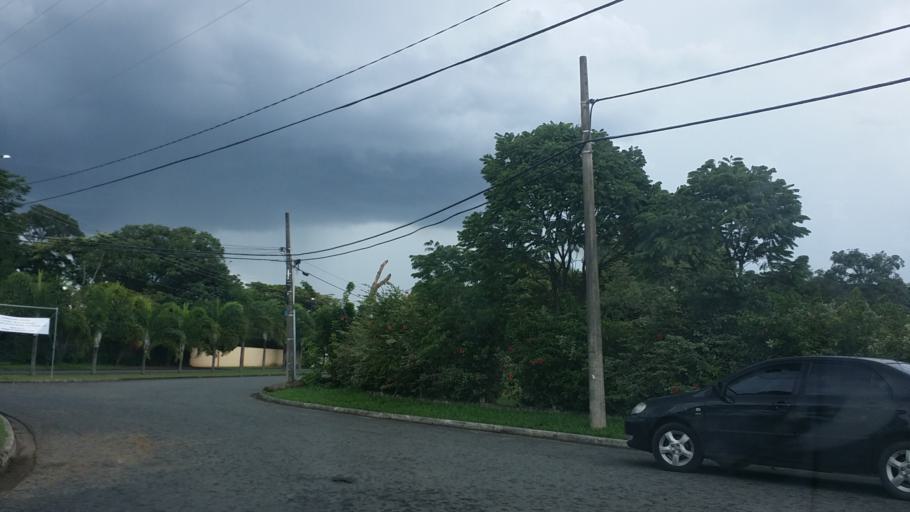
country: BR
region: Sao Paulo
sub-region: Indaiatuba
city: Indaiatuba
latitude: -23.1269
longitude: -47.1812
